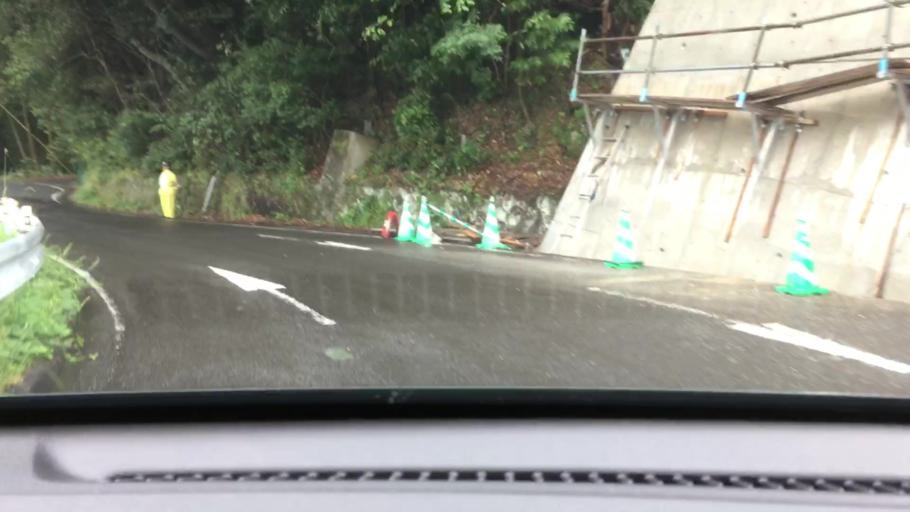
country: JP
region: Nagasaki
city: Togitsu
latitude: 32.8680
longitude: 129.7668
